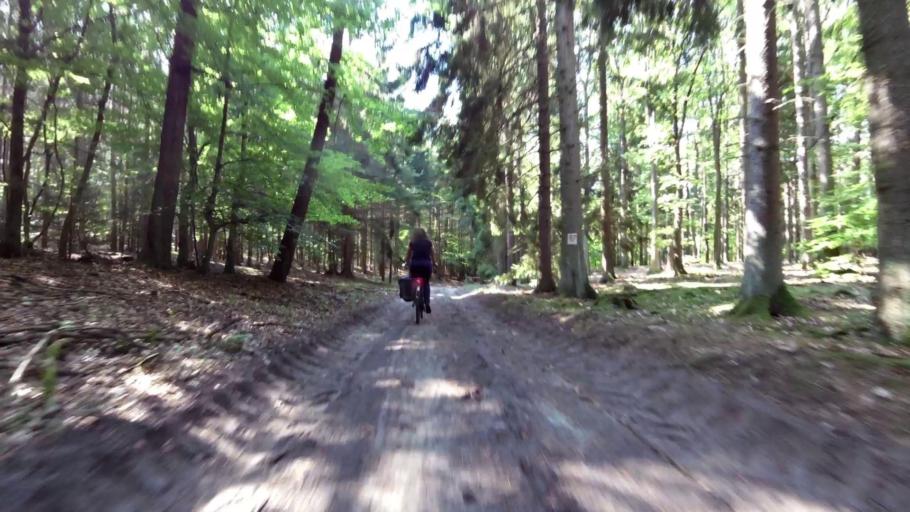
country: PL
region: West Pomeranian Voivodeship
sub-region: Powiat kamienski
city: Miedzyzdroje
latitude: 53.9130
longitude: 14.4917
